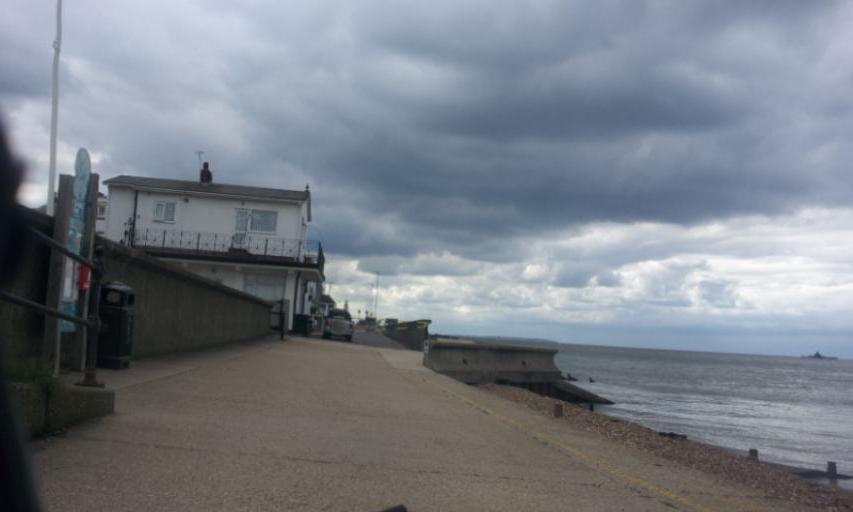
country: GB
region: England
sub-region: Kent
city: Herne Bay
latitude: 51.3729
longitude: 1.1362
